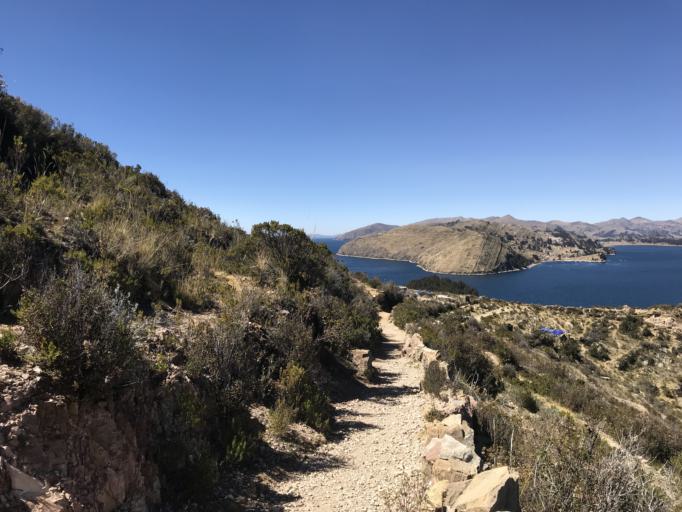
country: BO
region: La Paz
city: Yumani
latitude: -16.0438
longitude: -69.1468
